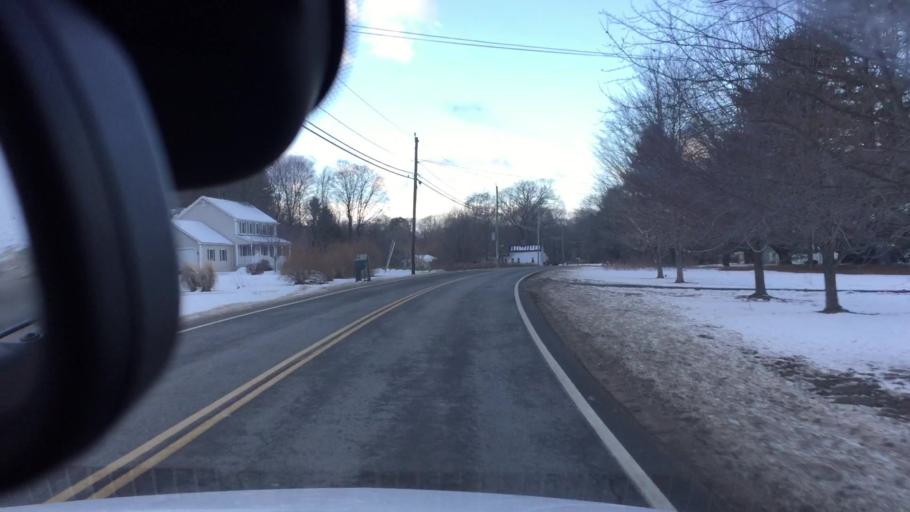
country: US
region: Massachusetts
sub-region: Franklin County
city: Montague
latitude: 42.4993
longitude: -72.5438
